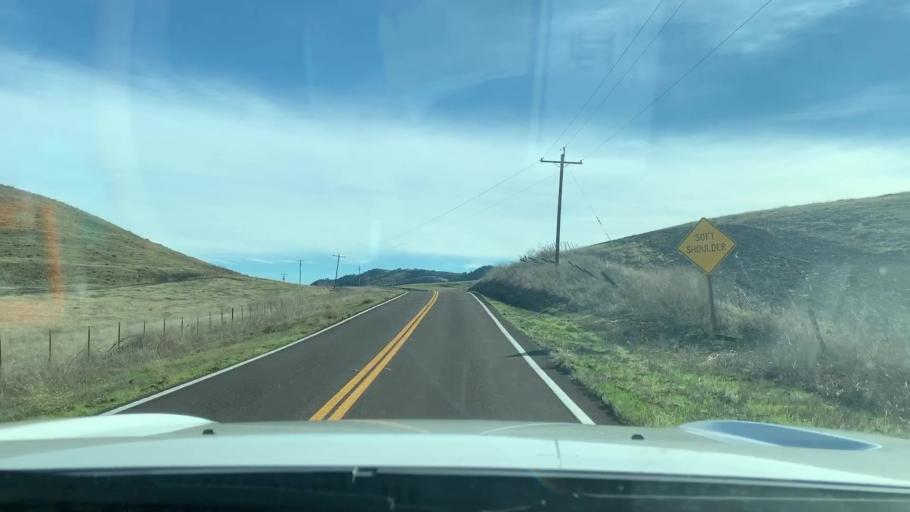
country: US
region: California
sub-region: Monterey County
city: King City
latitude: 36.1652
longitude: -120.8667
